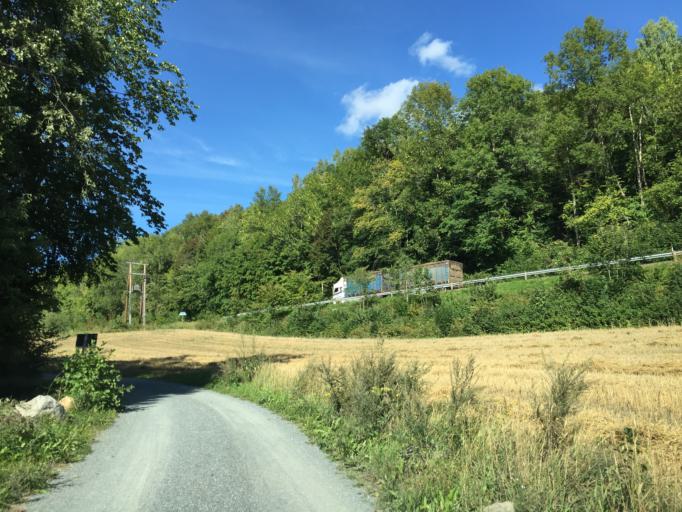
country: NO
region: Buskerud
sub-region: Ovre Eiker
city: Hokksund
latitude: 59.7041
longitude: 9.8638
